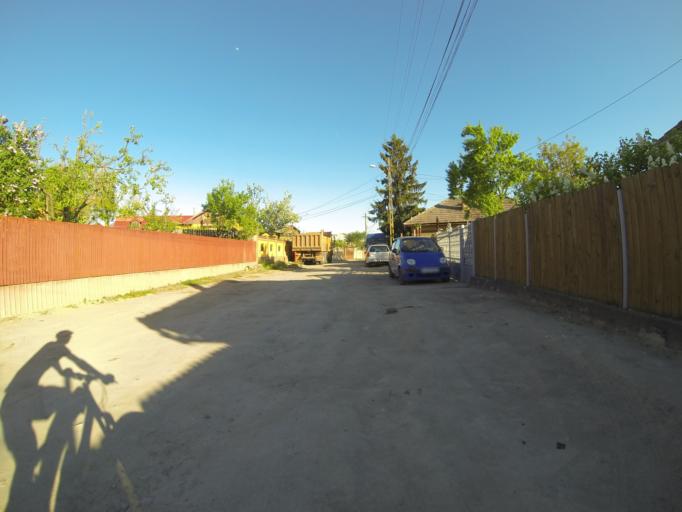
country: RO
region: Dolj
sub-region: Comuna Segarcea
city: Segarcea
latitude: 44.0933
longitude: 23.7406
